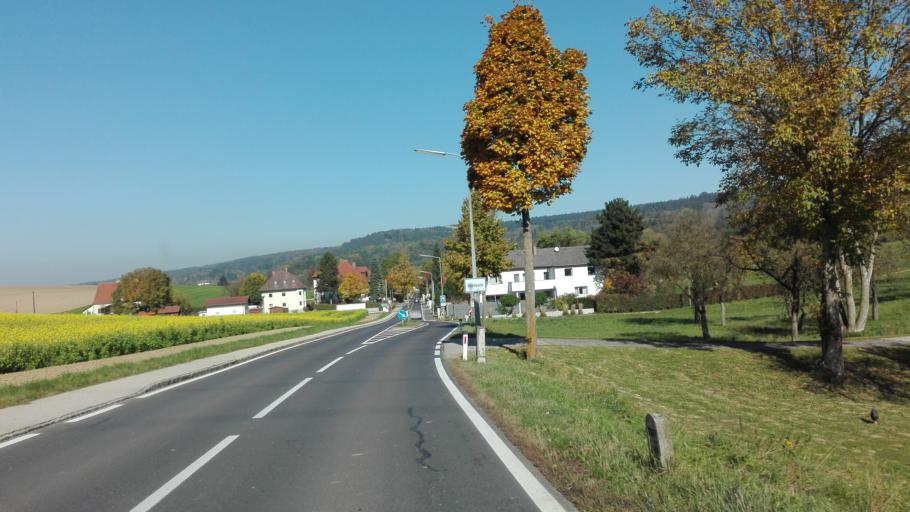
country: AT
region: Upper Austria
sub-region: Politischer Bezirk Linz-Land
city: Pasching
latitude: 48.2769
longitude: 14.2001
